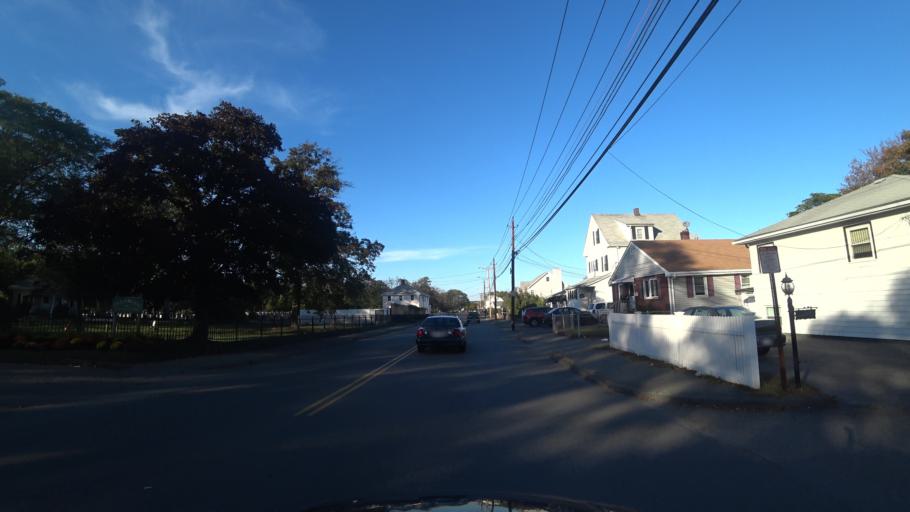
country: US
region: Massachusetts
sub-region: Suffolk County
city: Revere
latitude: 42.4195
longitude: -71.0307
